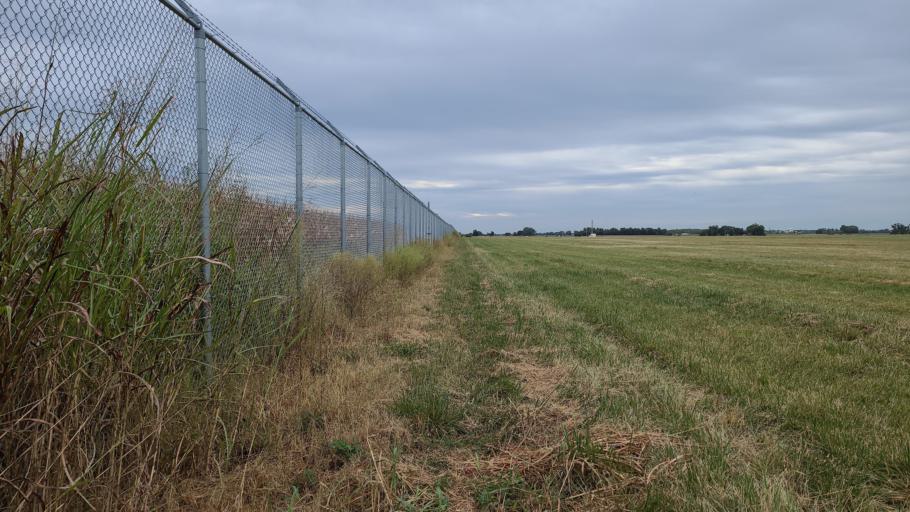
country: US
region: Kansas
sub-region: Douglas County
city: Lawrence
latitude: 39.0123
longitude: -95.2131
